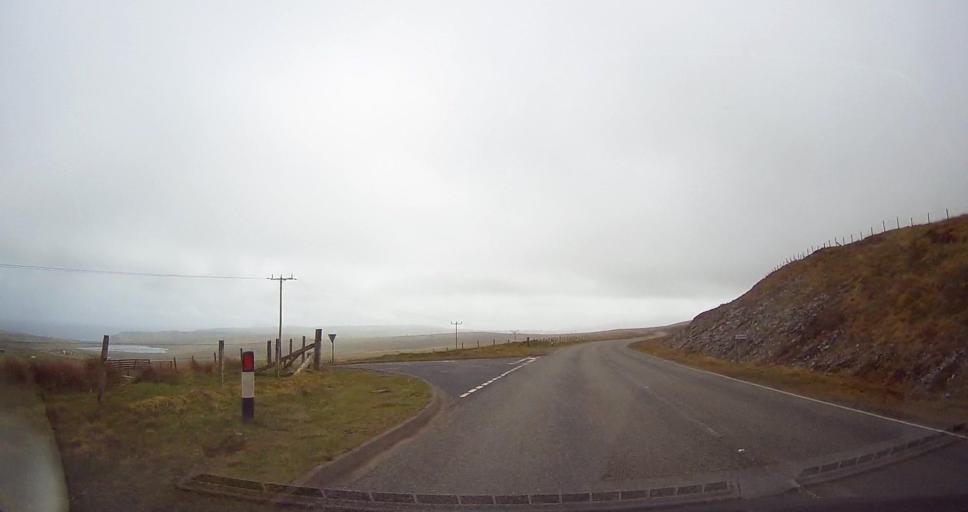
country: GB
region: Scotland
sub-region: Shetland Islands
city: Sandwick
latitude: 59.9567
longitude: -1.2871
